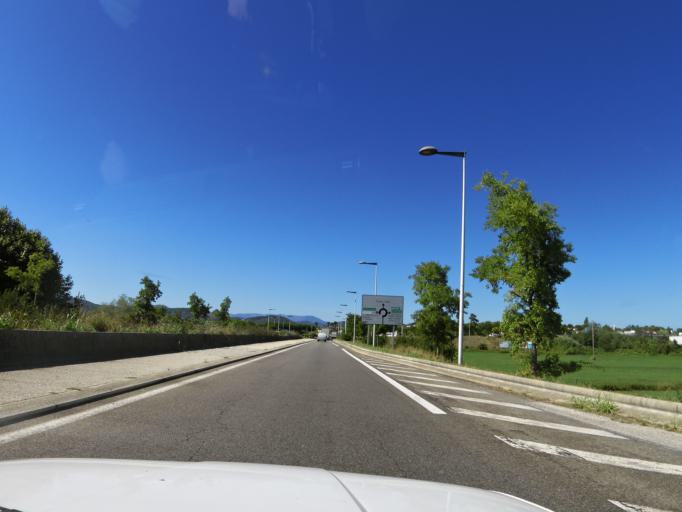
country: FR
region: Languedoc-Roussillon
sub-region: Departement du Gard
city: Ales
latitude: 44.1054
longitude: 4.1003
